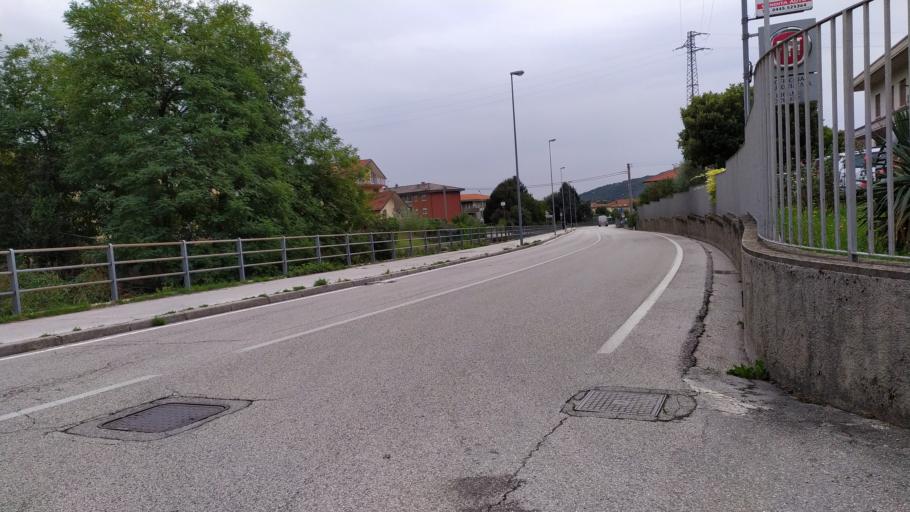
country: IT
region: Veneto
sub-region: Provincia di Vicenza
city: Torrebelvicino
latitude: 45.7186
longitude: 11.3333
